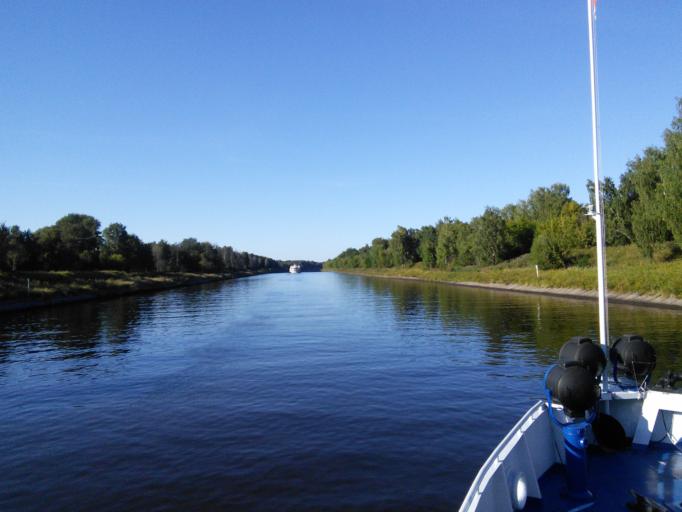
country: RU
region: Moskovskaya
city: Yakhroma
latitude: 56.3041
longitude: 37.4892
